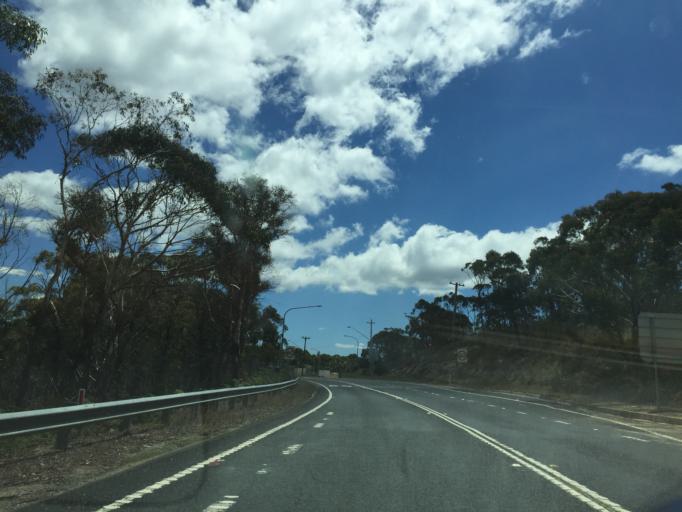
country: AU
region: New South Wales
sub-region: Blue Mountains Municipality
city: Blackheath
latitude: -33.5123
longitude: 150.2870
